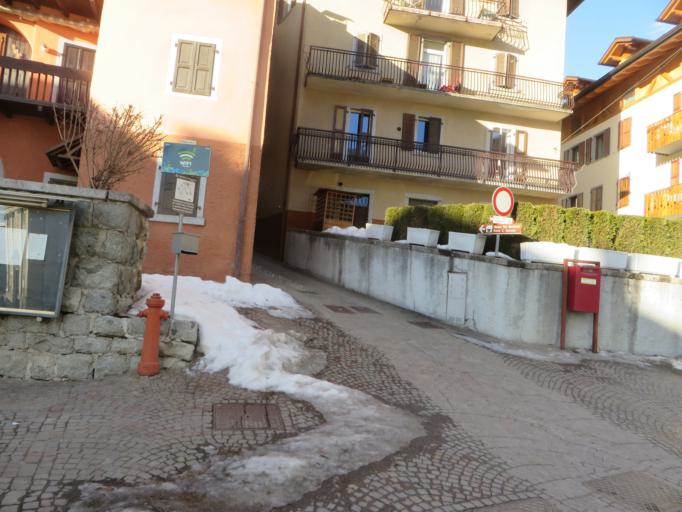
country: IT
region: Trentino-Alto Adige
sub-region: Provincia di Trento
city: Caderzone Terme
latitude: 46.1297
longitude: 10.7572
